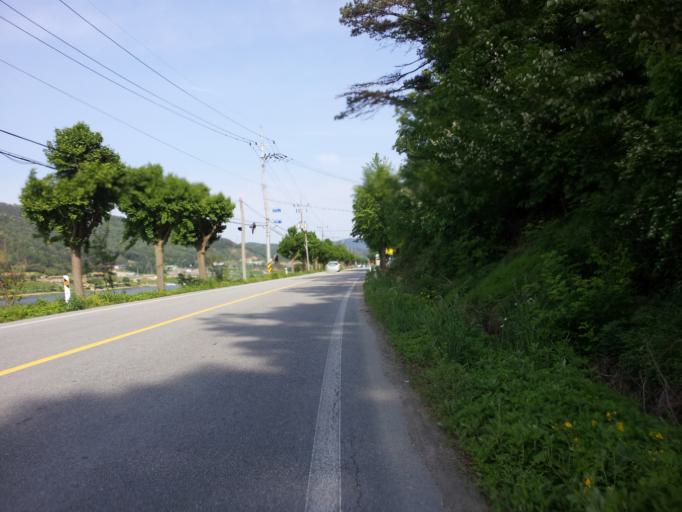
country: KR
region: Chungcheongnam-do
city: Gongju
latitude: 36.4451
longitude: 127.1814
